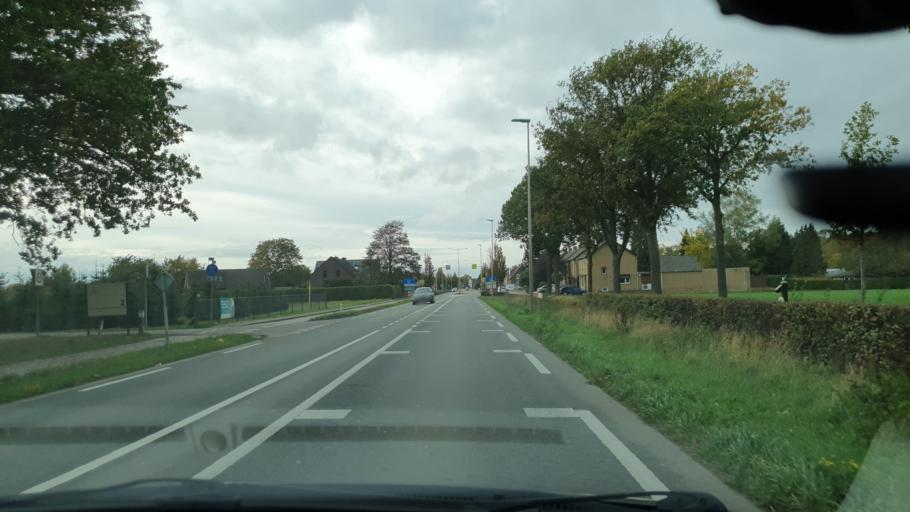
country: NL
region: Limburg
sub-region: Gemeente Roerdalen
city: Montfort
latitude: 51.0904
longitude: 5.9109
